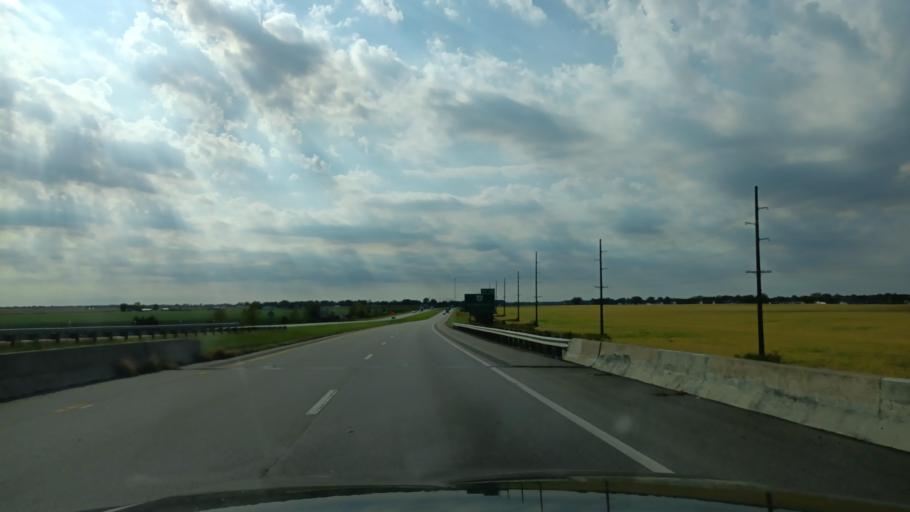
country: US
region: Ohio
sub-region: Fayette County
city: Washington Court House
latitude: 39.5128
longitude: -83.4182
